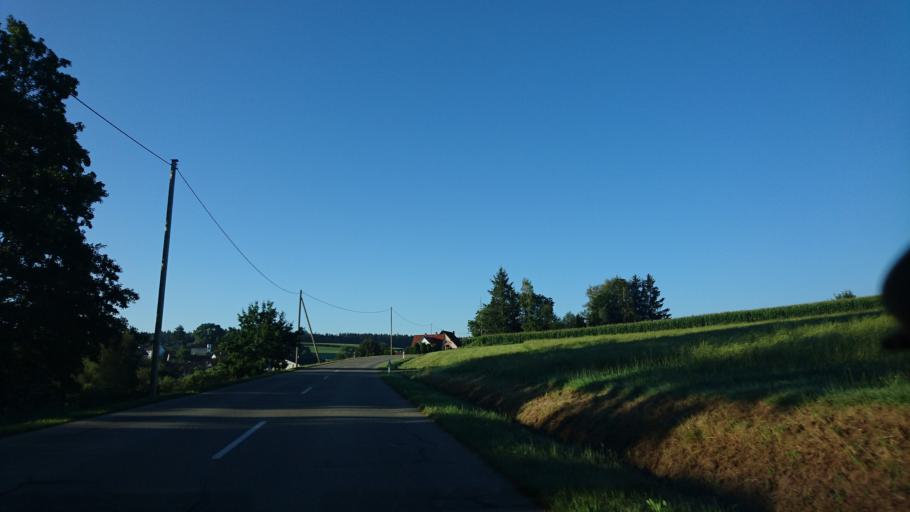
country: DE
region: Bavaria
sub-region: Swabia
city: Grossaitingen
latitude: 48.2383
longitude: 10.7317
